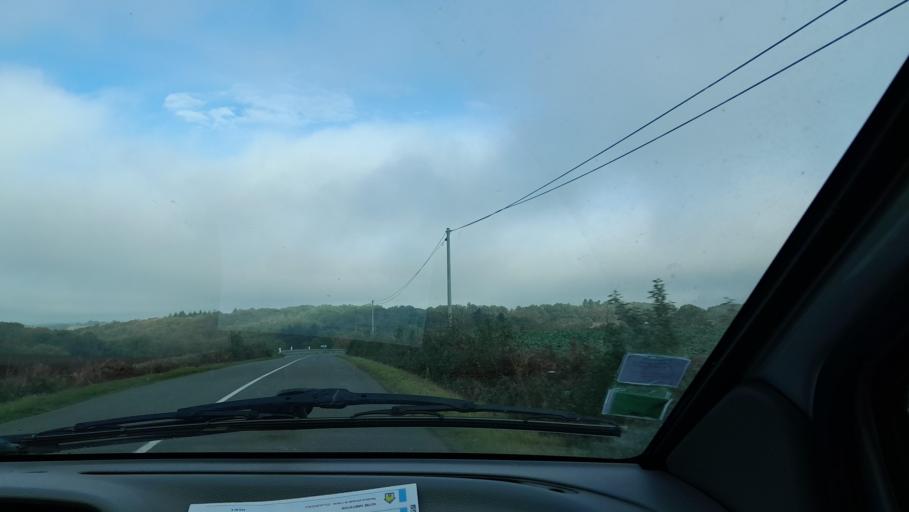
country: FR
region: Brittany
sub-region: Departement d'Ille-et-Vilaine
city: Luitre
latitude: 48.2531
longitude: -1.1263
